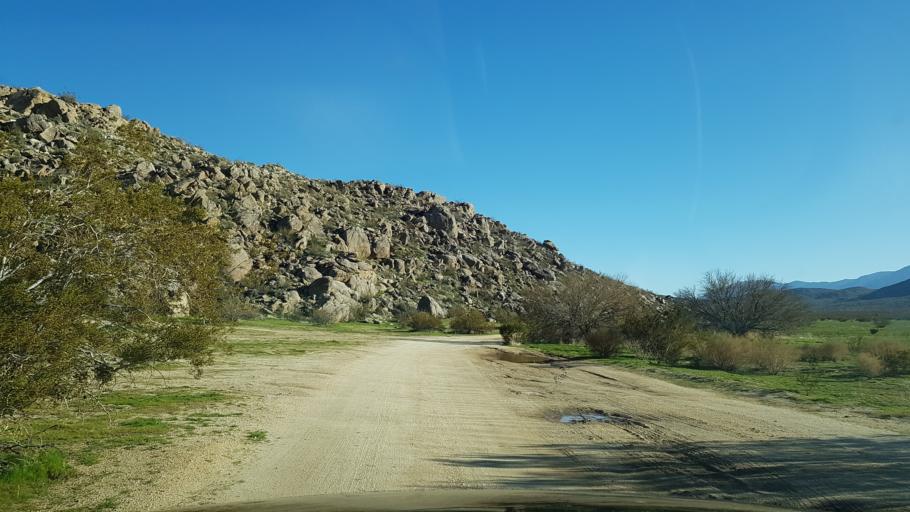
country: US
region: California
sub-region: San Diego County
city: Julian
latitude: 33.0318
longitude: -116.3993
